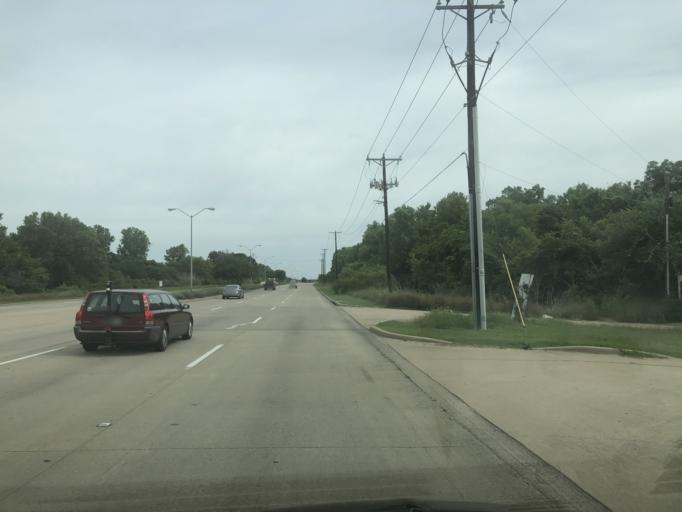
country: US
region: Texas
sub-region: Dallas County
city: Grand Prairie
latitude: 32.7848
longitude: -96.9946
